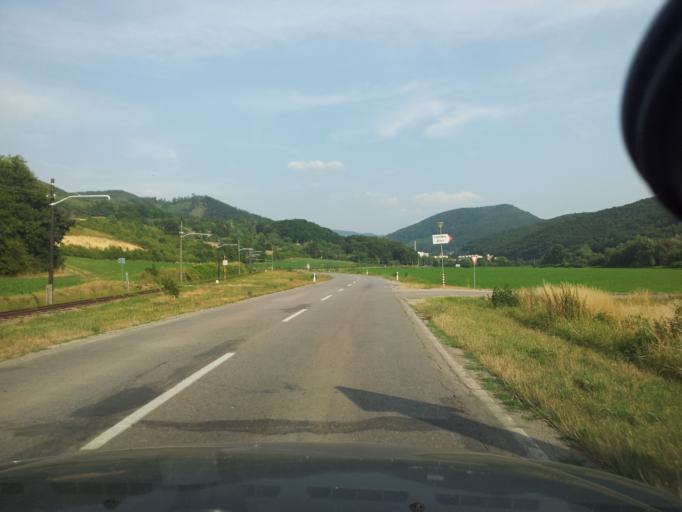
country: SK
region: Trenciansky
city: Nova Dubnica
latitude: 48.9212
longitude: 18.1453
